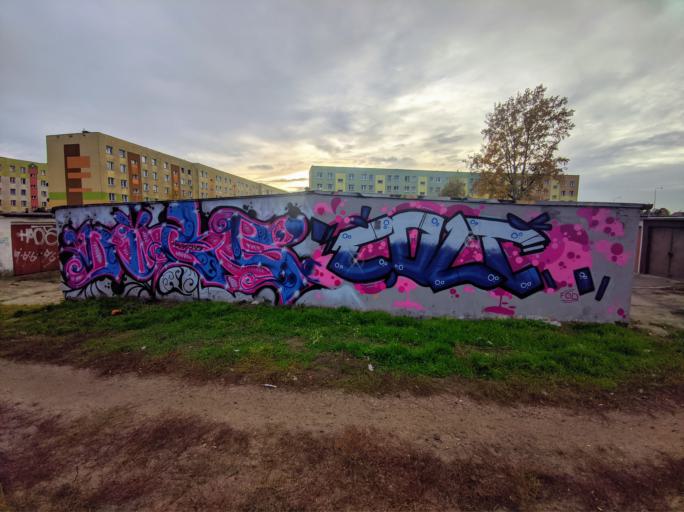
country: PL
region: Lubusz
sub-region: Powiat nowosolski
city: Nowa Sol
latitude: 51.8080
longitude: 15.7027
